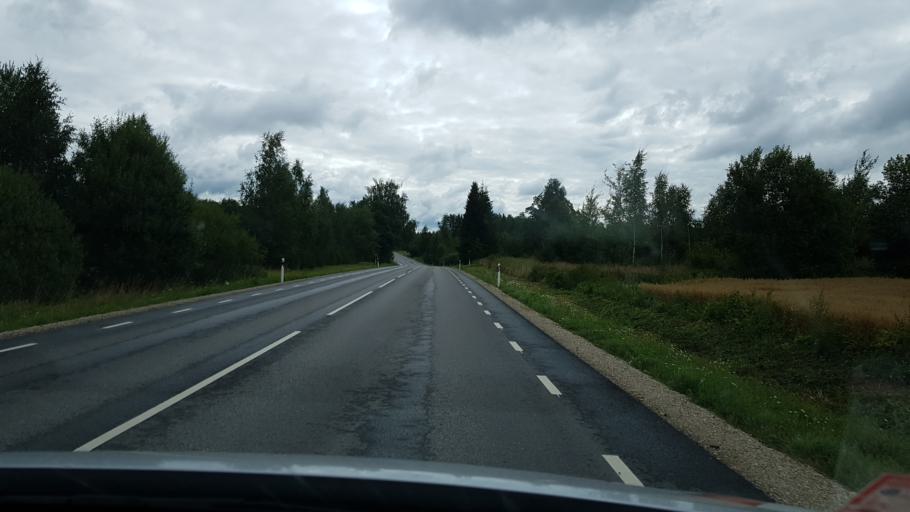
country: EE
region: Polvamaa
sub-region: Polva linn
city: Polva
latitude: 58.0115
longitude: 27.1807
